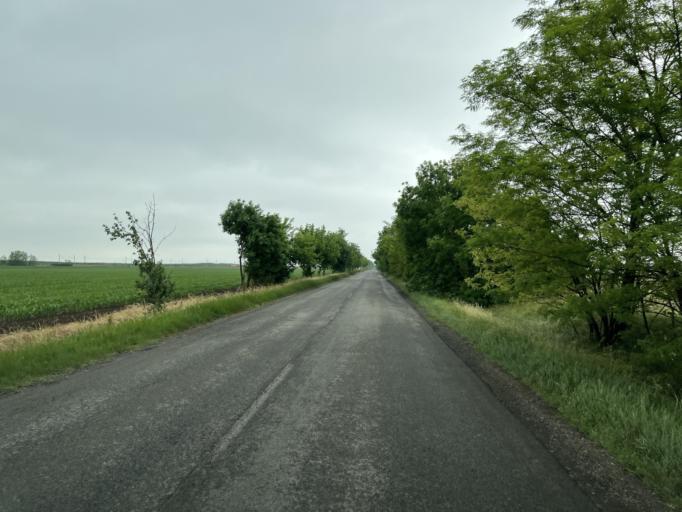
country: HU
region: Pest
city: Tura
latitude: 47.6252
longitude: 19.6205
